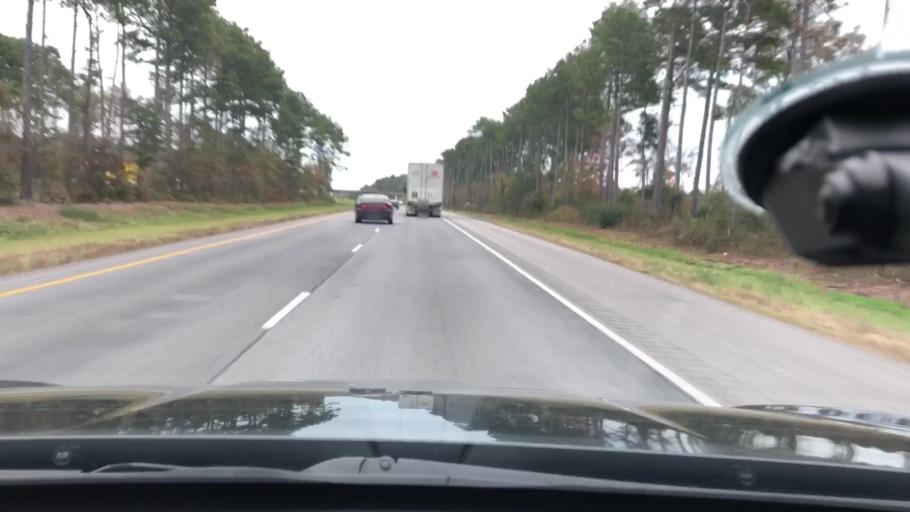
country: US
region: Arkansas
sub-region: Hempstead County
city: Hope
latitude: 33.6285
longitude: -93.7341
